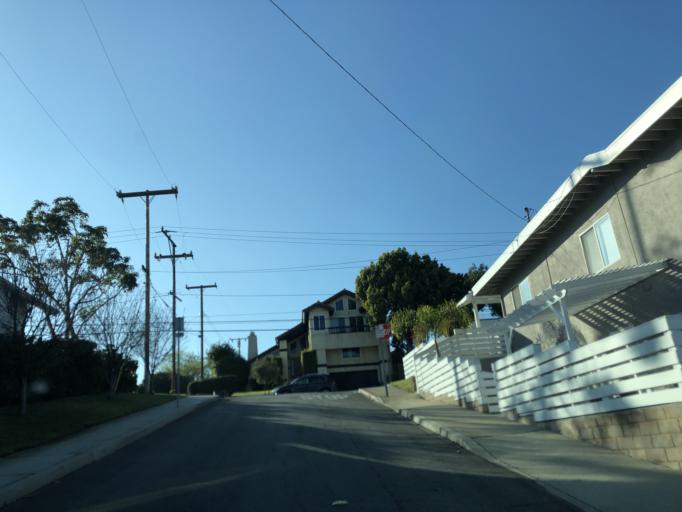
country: US
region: California
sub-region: Los Angeles County
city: El Segundo
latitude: 33.9281
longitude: -118.4109
